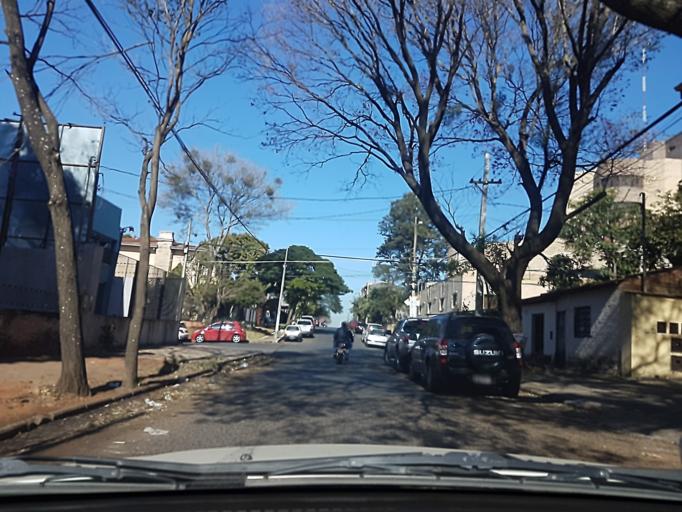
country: PY
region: Central
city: Lambare
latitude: -25.3199
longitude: -57.5908
